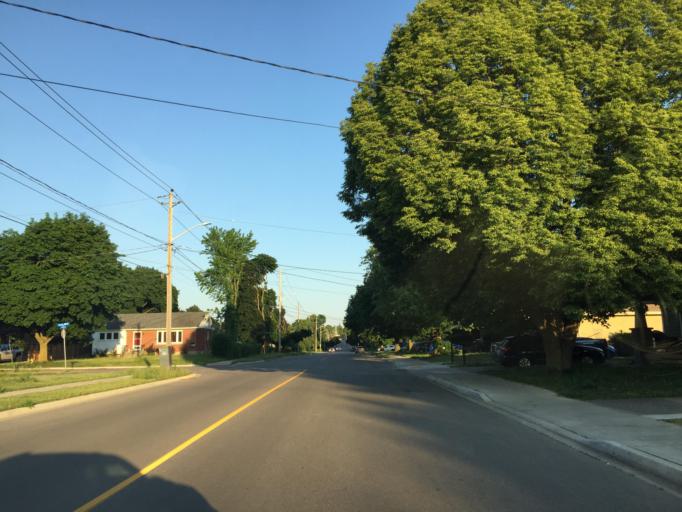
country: CA
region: Ontario
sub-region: Wellington County
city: Guelph
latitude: 43.5608
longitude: -80.2548
